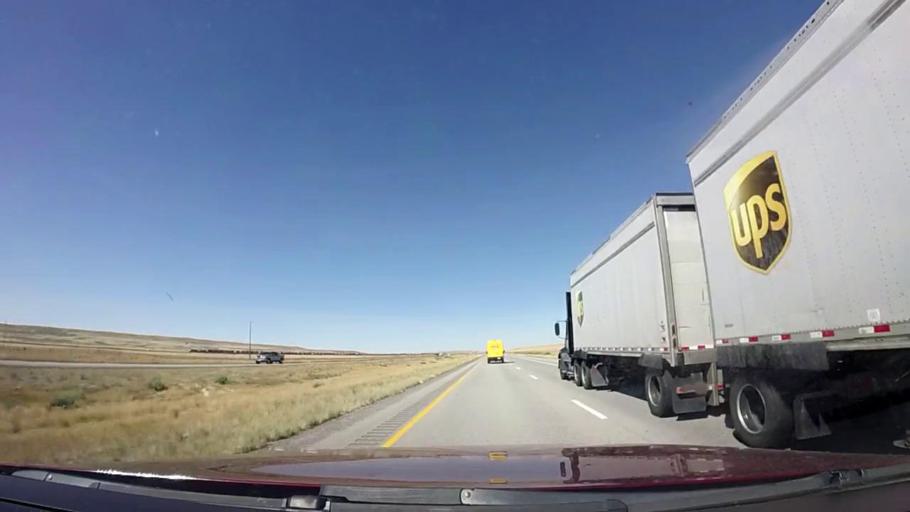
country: US
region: Wyoming
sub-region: Carbon County
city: Rawlins
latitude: 41.6596
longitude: -108.0762
